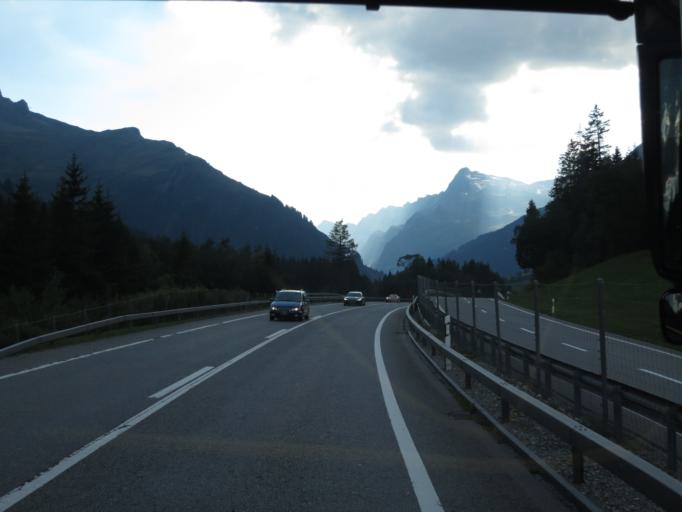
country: CH
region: Grisons
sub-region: Hinterrhein District
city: Hinterrhein
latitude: 46.5412
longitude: 9.2742
